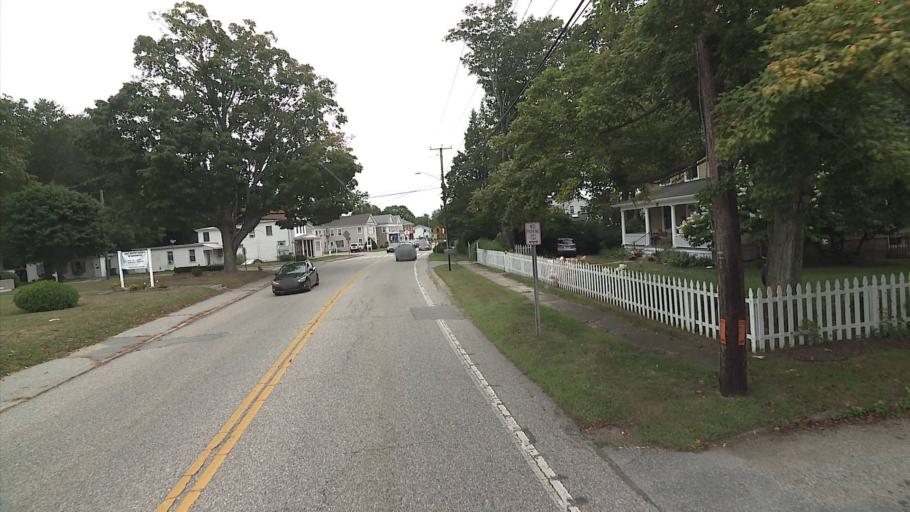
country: US
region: Connecticut
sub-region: New London County
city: Central Waterford
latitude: 41.3397
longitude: -72.1432
